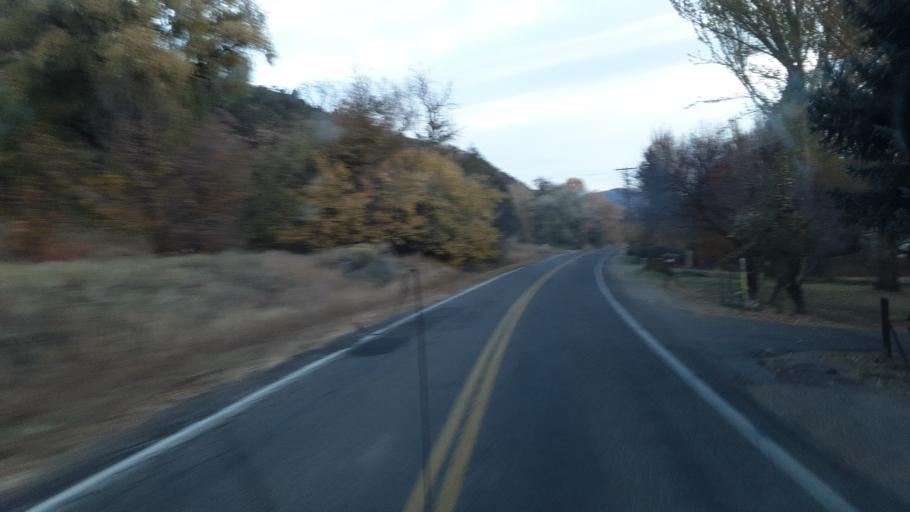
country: US
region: Colorado
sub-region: La Plata County
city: Durango
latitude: 37.3488
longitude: -107.8577
